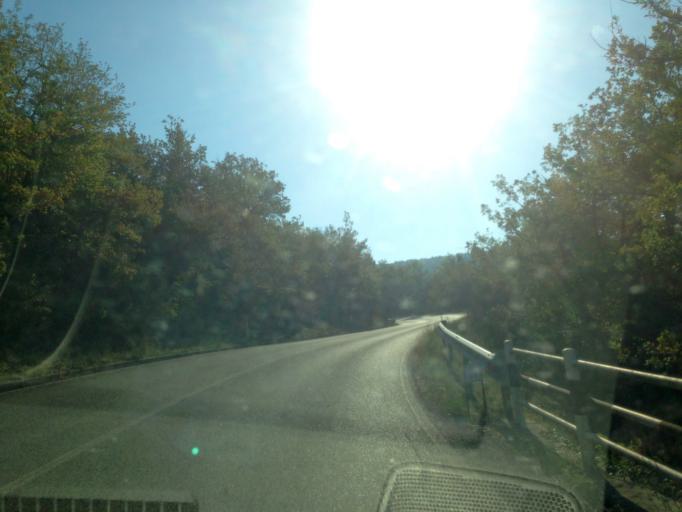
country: IT
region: Tuscany
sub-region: Provincia di Siena
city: Castellina in Chianti
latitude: 43.5042
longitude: 11.2941
